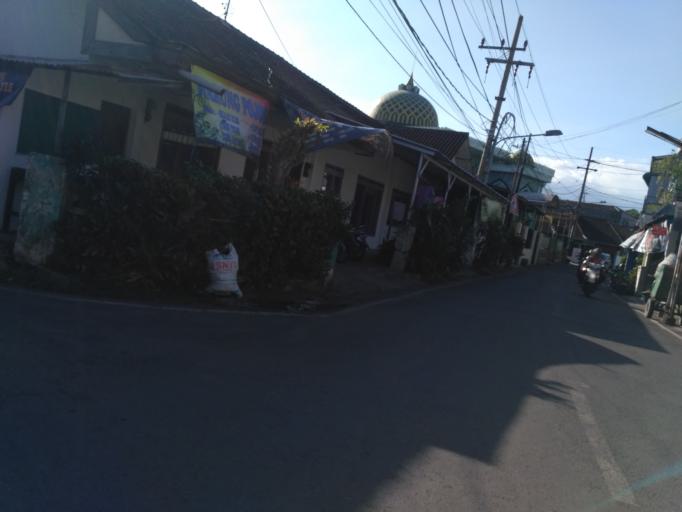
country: ID
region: East Java
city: Malang
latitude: -7.9372
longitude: 112.6023
